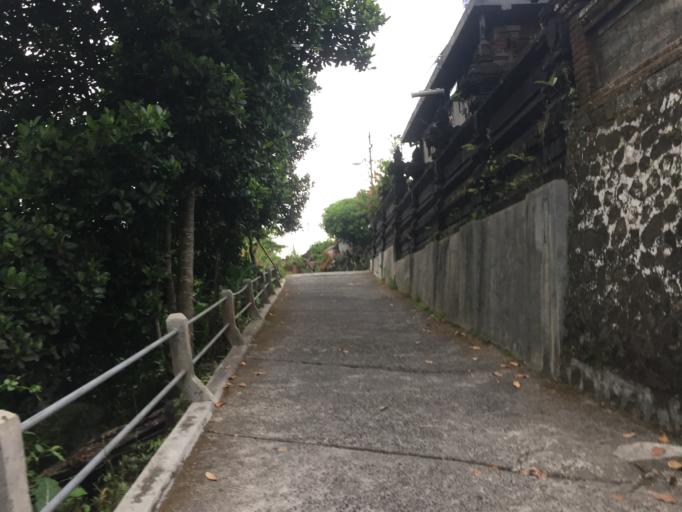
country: ID
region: Bali
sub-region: Kabupaten Gianyar
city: Ubud
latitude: -8.5049
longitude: 115.2568
